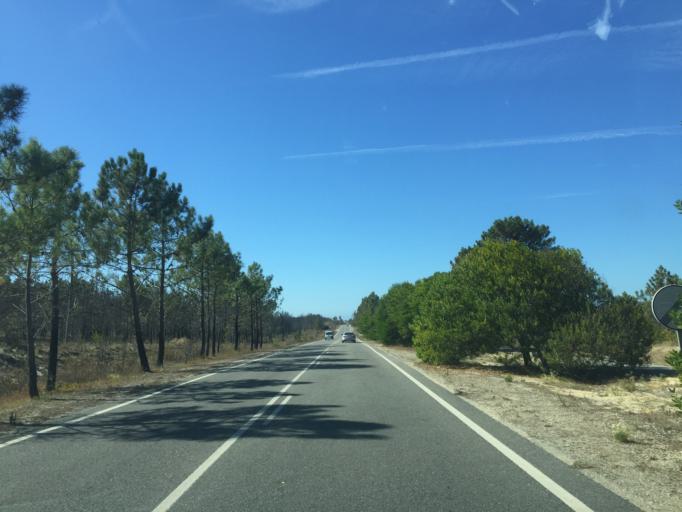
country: PT
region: Coimbra
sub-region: Mira
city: Mira
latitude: 40.3256
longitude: -8.8145
